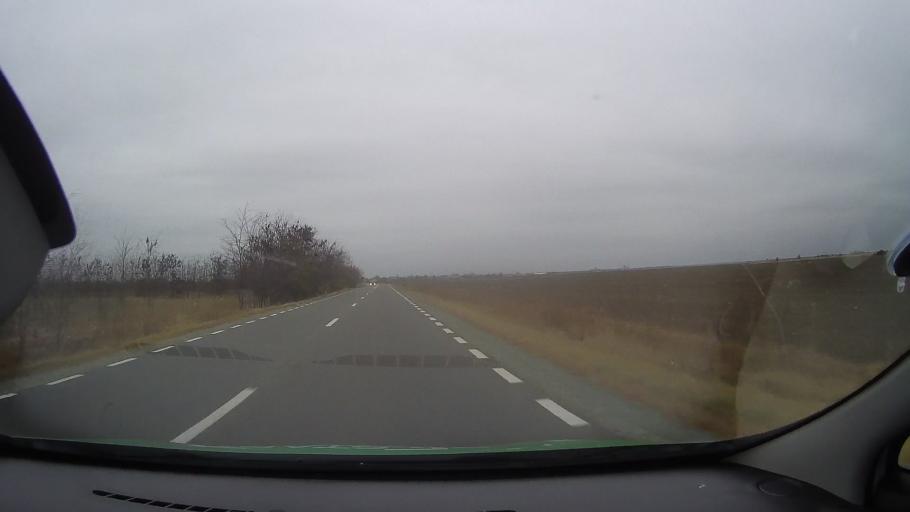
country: RO
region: Ialomita
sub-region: Comuna Slobozia
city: Slobozia
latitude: 44.6127
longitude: 27.3858
